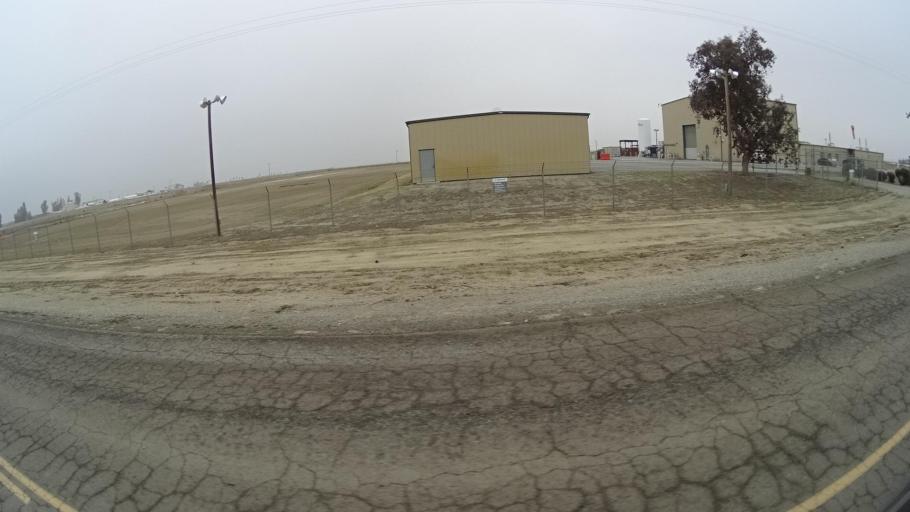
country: US
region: California
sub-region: Kern County
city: Maricopa
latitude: 35.1471
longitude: -119.2400
